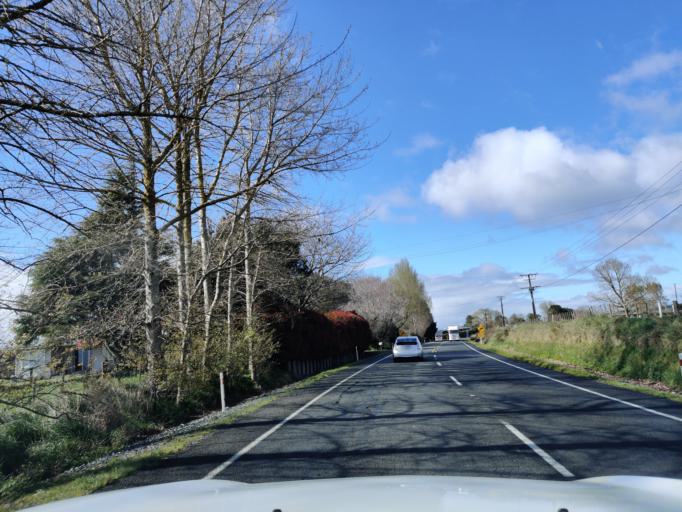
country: NZ
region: Waikato
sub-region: Otorohanga District
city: Otorohanga
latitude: -38.0974
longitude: 175.1884
